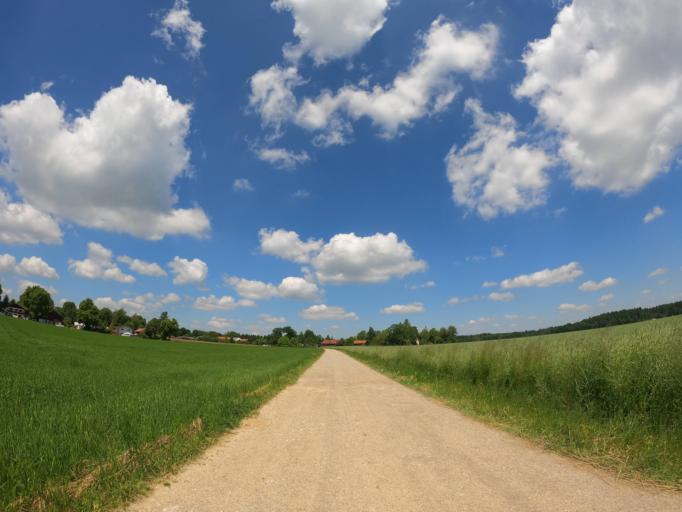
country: DE
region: Bavaria
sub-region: Upper Bavaria
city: Oberhaching
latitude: 47.9889
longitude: 11.5642
